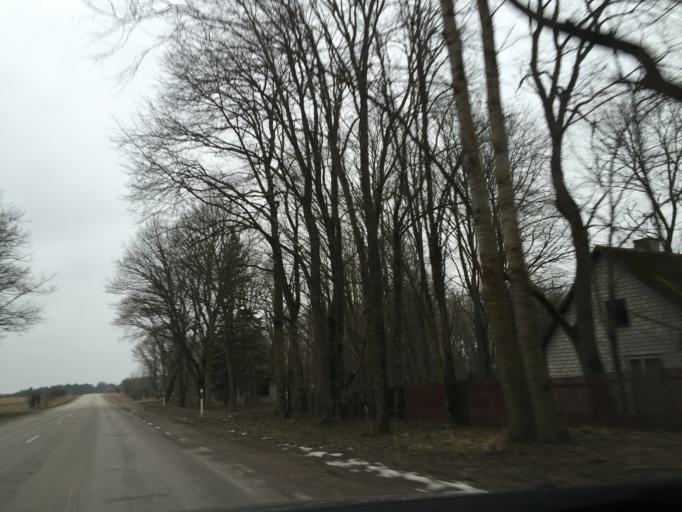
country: EE
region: Saare
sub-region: Kuressaare linn
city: Kuressaare
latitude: 58.2905
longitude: 22.2901
